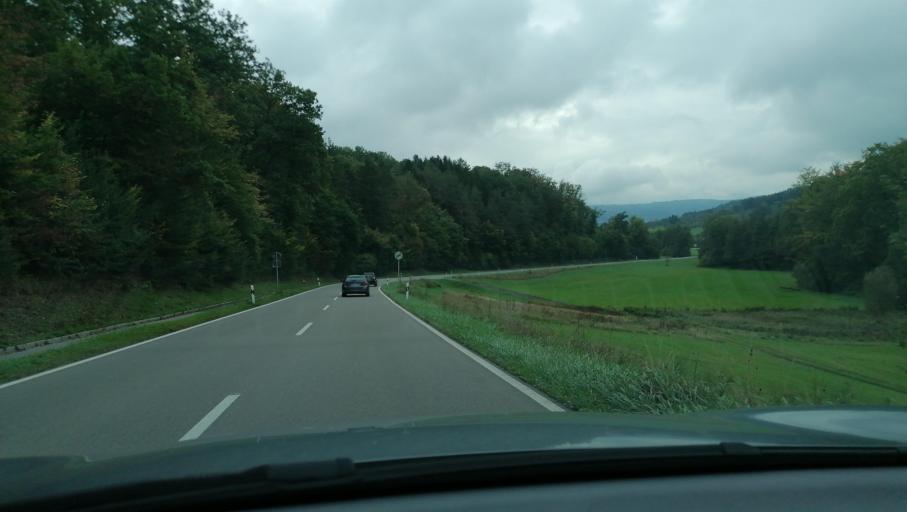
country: DE
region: Baden-Wuerttemberg
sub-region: Regierungsbezirk Stuttgart
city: Winterbach
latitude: 48.8427
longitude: 9.4958
